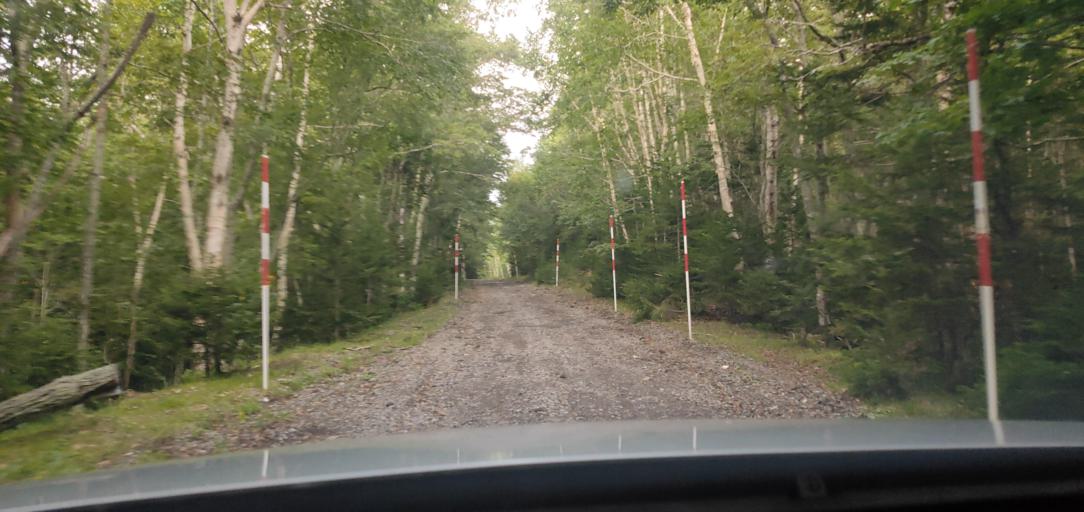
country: JP
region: Hokkaido
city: Kitami
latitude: 43.3751
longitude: 143.9672
